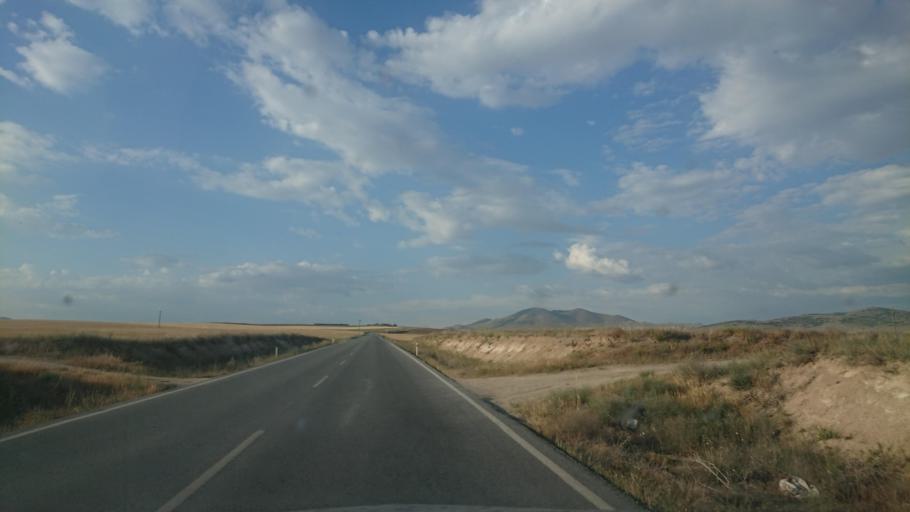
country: TR
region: Aksaray
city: Aksaray
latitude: 38.4913
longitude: 34.0707
